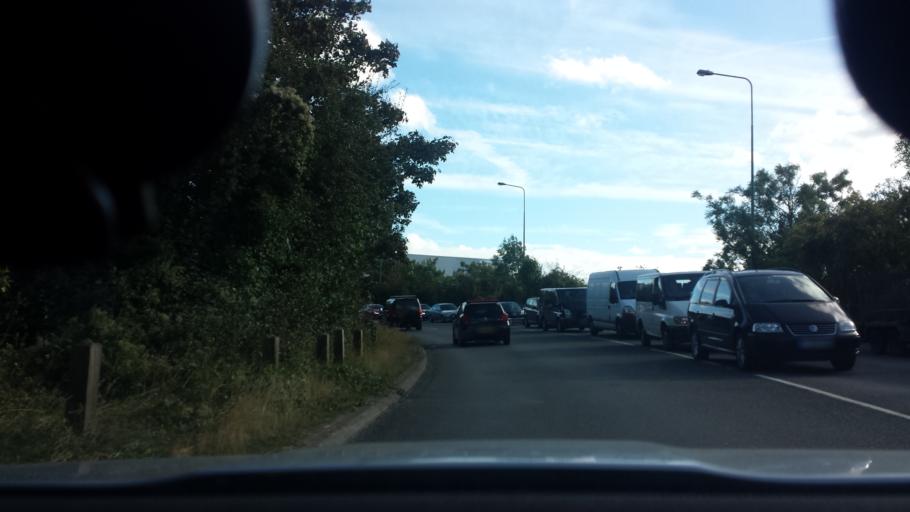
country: GB
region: England
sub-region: Kent
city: Swanley
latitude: 51.3889
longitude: 0.1880
